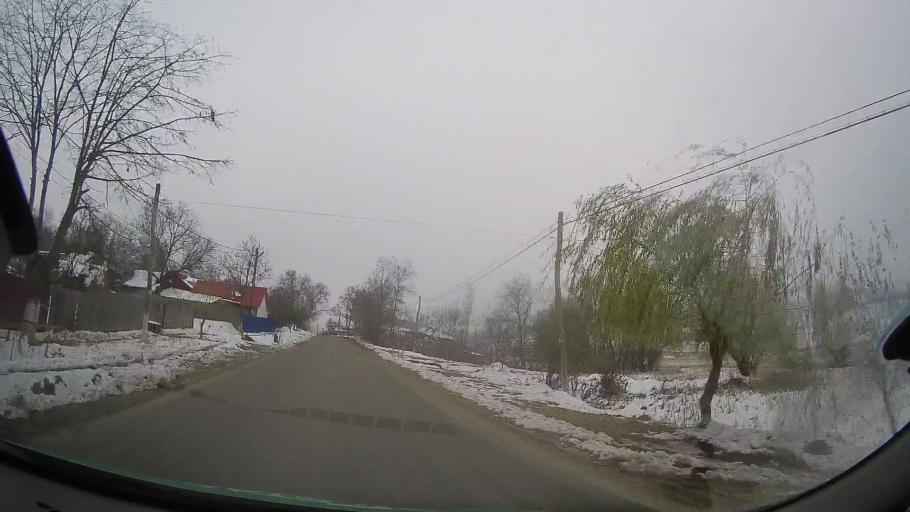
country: RO
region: Bacau
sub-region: Comuna Glavanesti
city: Frumuselu
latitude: 46.2894
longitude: 27.3008
